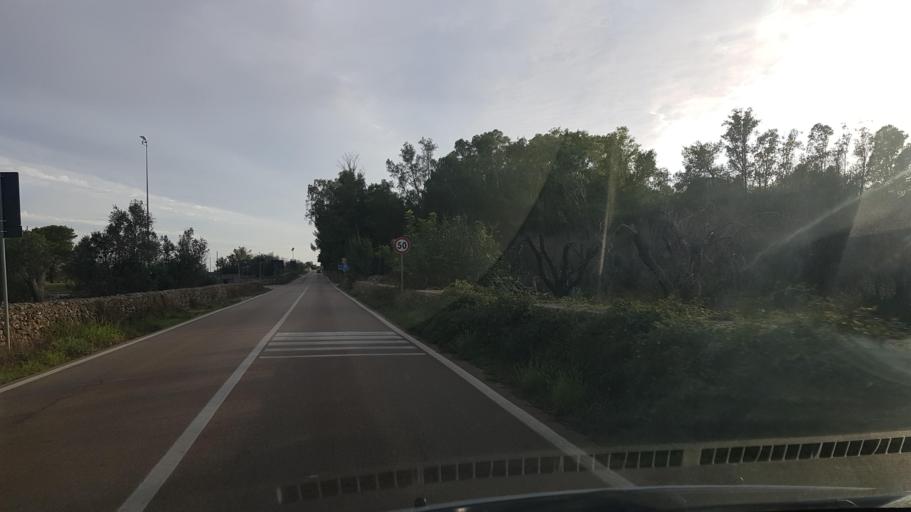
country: IT
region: Apulia
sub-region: Provincia di Lecce
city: Trepuzzi
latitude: 40.4598
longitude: 18.1151
